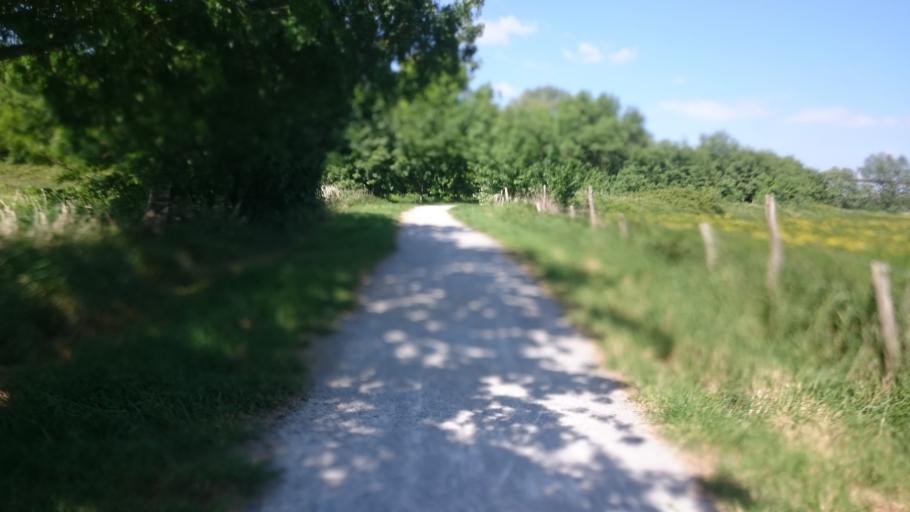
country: FR
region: Pays de la Loire
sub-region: Departement de la Loire-Atlantique
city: Bouguenais
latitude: 47.1836
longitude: -1.6238
